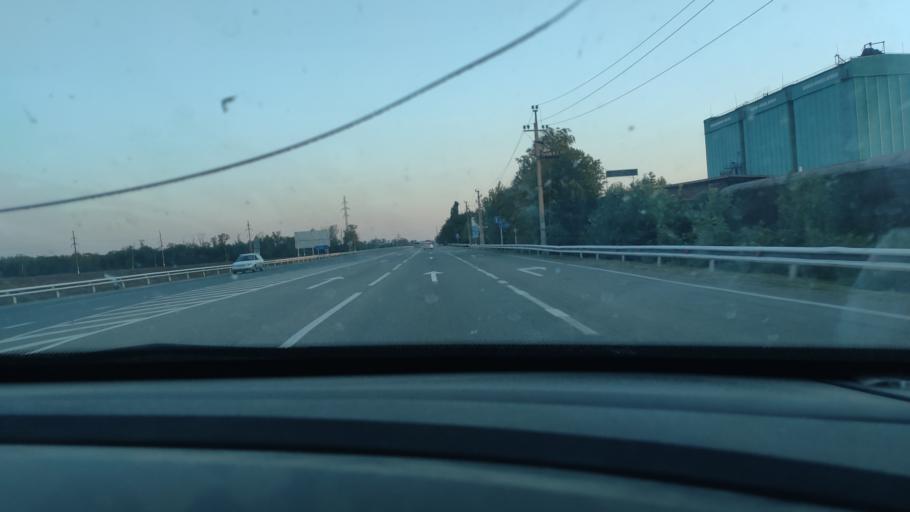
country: RU
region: Krasnodarskiy
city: Timashevsk
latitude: 45.6220
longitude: 38.9863
